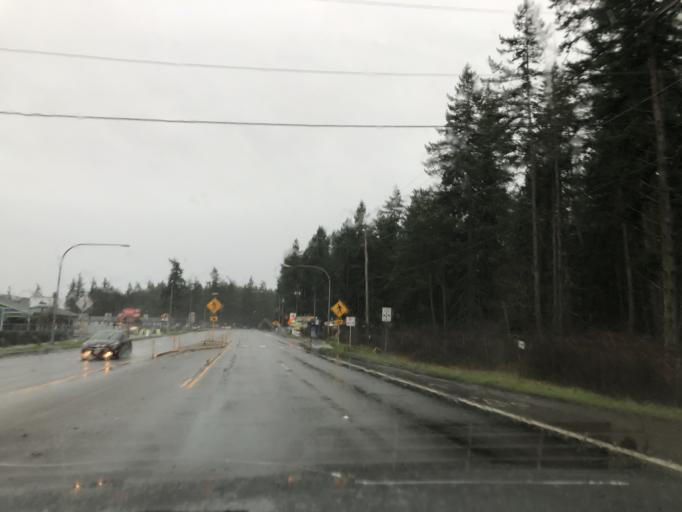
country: US
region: Washington
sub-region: Pierce County
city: Spanaway
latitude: 47.0863
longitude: -122.4353
